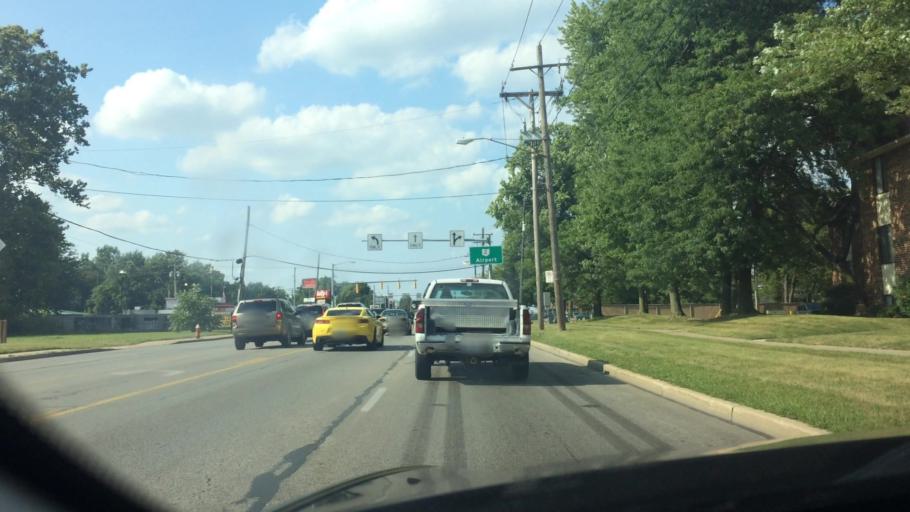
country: US
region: Ohio
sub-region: Lucas County
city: Ottawa Hills
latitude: 41.6227
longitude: -83.6258
